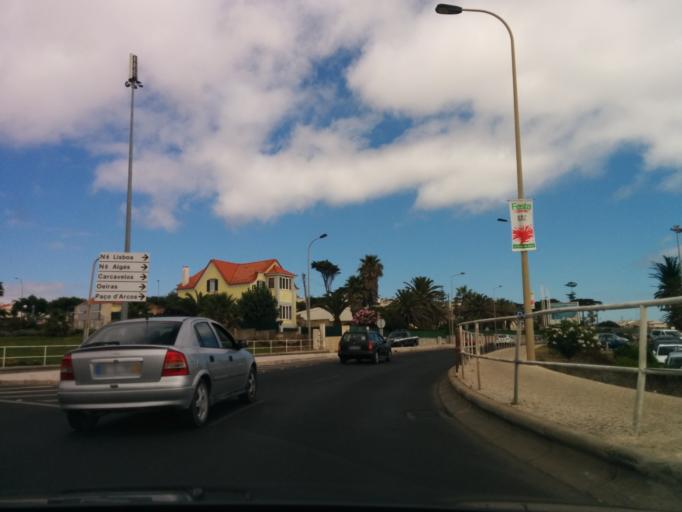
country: PT
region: Lisbon
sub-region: Cascais
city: Parede
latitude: 38.6929
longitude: -9.3671
